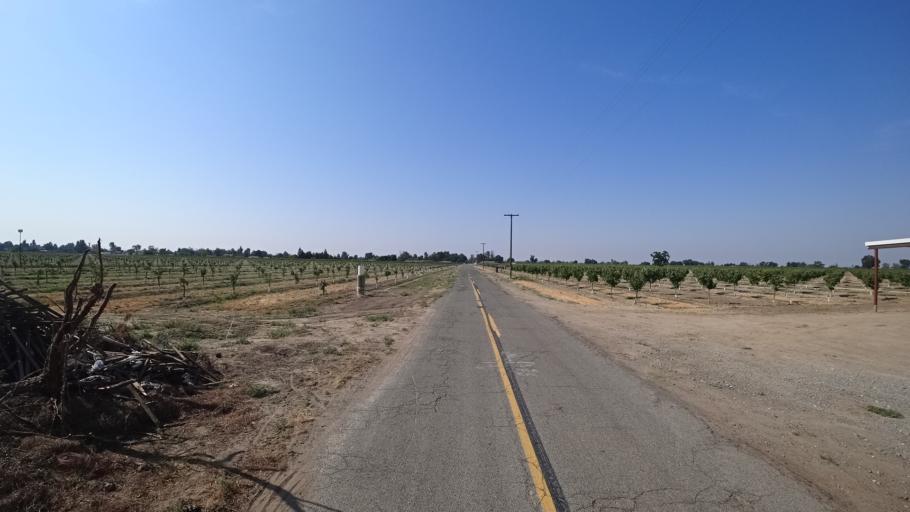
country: US
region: California
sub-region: Fresno County
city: Riverdale
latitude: 36.3581
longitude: -119.8430
